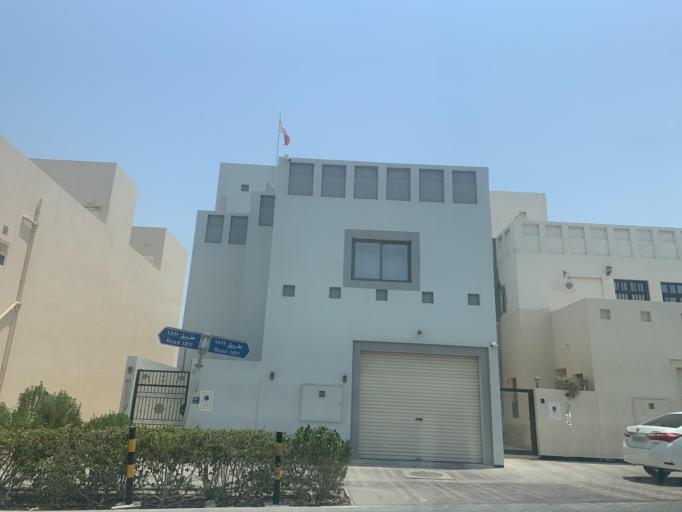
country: BH
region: Muharraq
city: Al Hadd
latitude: 26.2367
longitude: 50.6729
